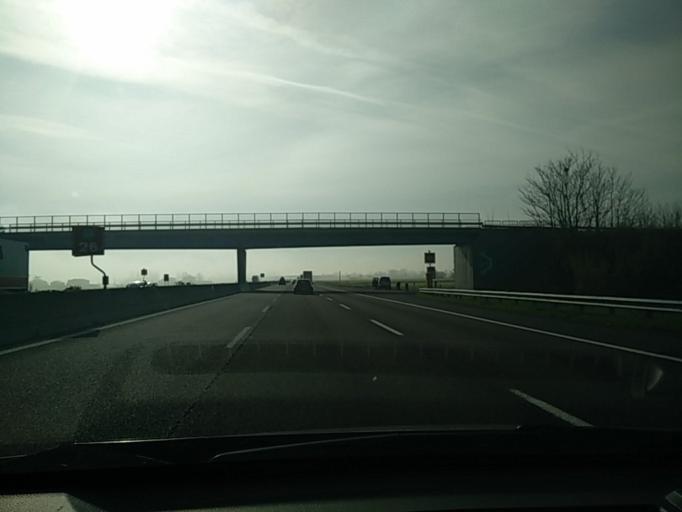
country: IT
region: Emilia-Romagna
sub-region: Provincia di Bologna
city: Osteria Grande
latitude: 44.4494
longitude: 11.5439
